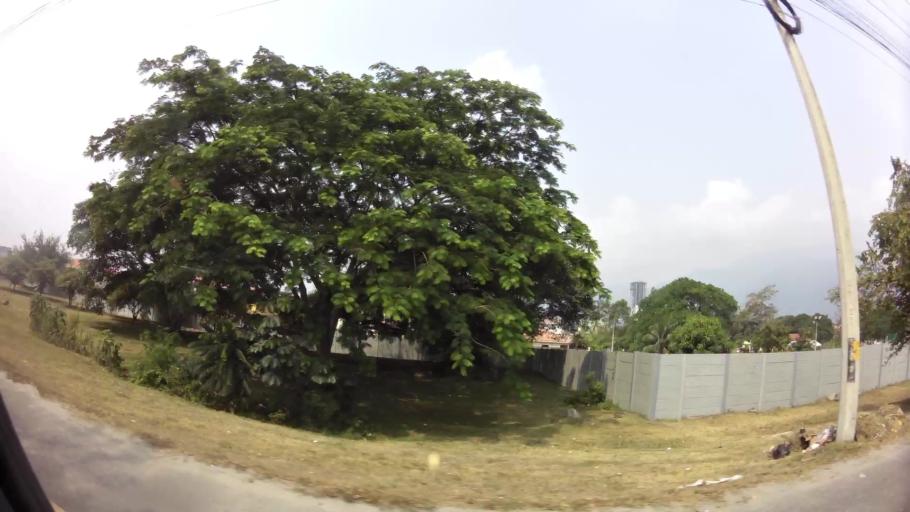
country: HN
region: Cortes
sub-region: San Pedro Sula
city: Pena Blanca
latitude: 15.5557
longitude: -88.0145
